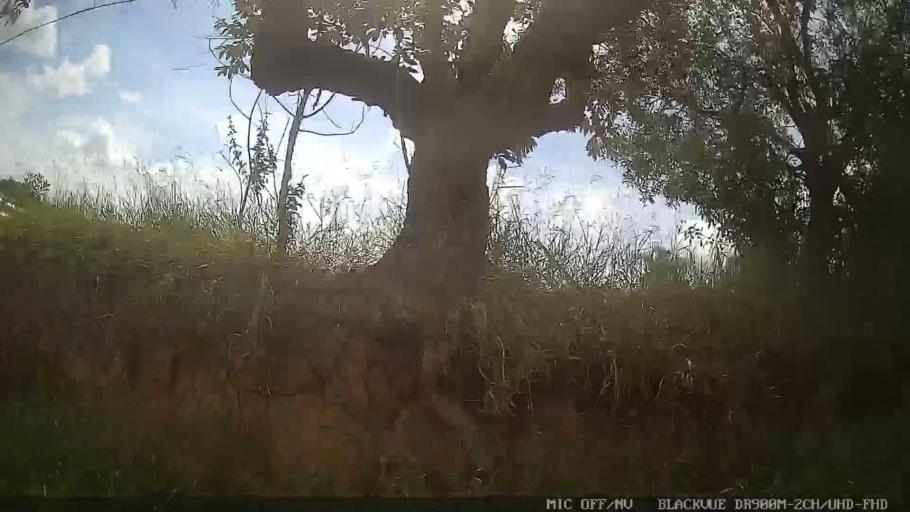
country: BR
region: Sao Paulo
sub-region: Atibaia
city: Atibaia
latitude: -23.0927
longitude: -46.5529
